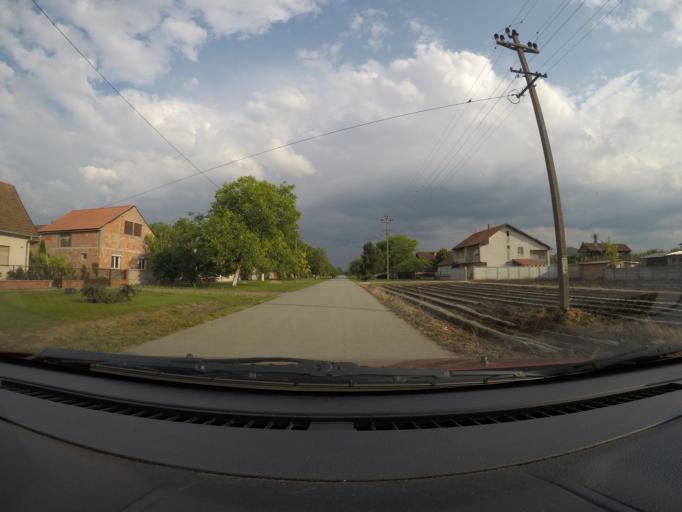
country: RS
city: Debeljaca
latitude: 45.0773
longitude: 20.5988
